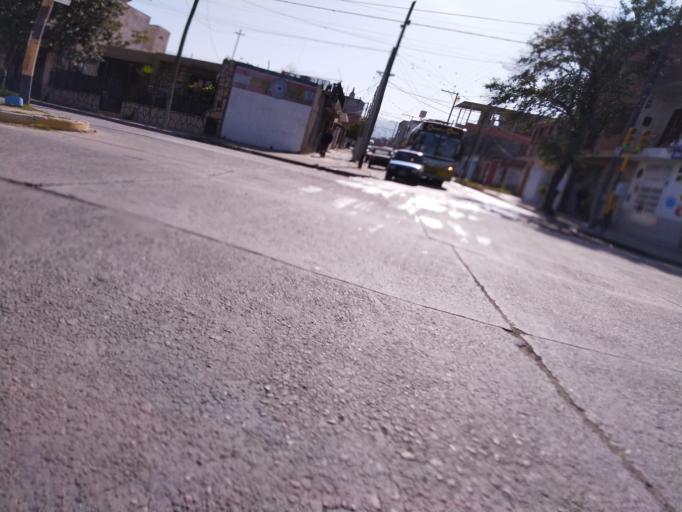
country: AR
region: Jujuy
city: San Salvador de Jujuy
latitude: -24.1987
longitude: -65.2799
